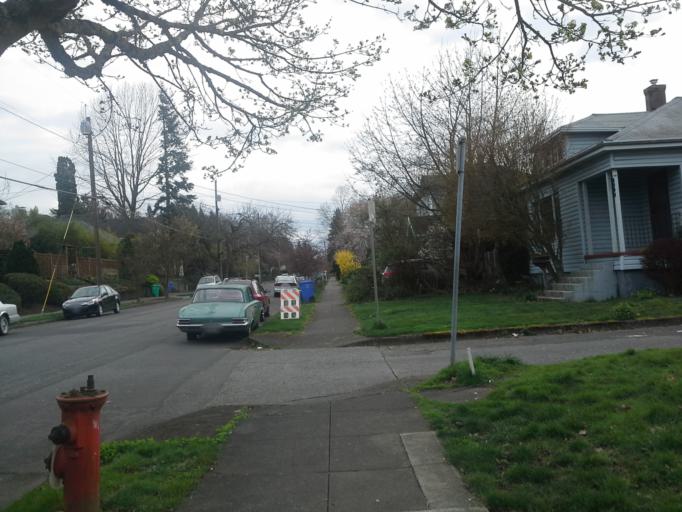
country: US
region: Oregon
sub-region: Clackamas County
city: Milwaukie
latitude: 45.4947
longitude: -122.6268
